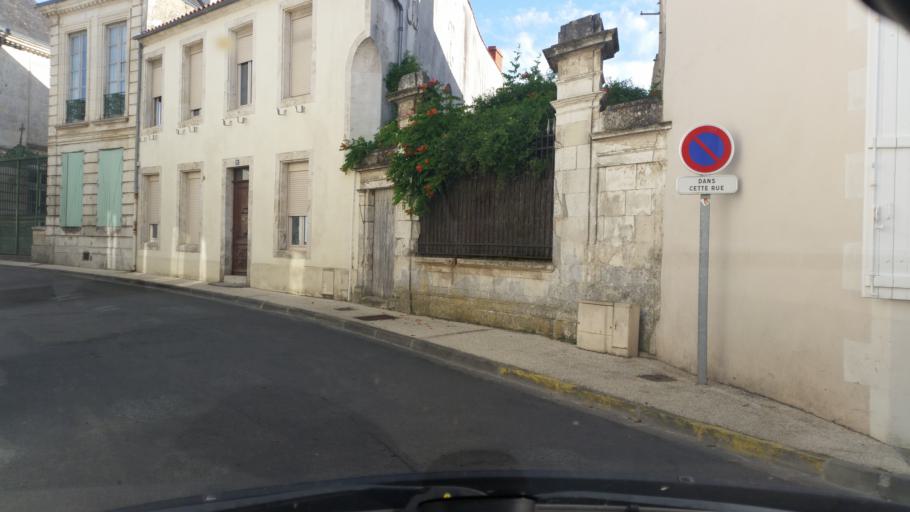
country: FR
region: Poitou-Charentes
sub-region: Departement de la Charente-Maritime
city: Marans
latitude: 46.3089
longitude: -0.9944
